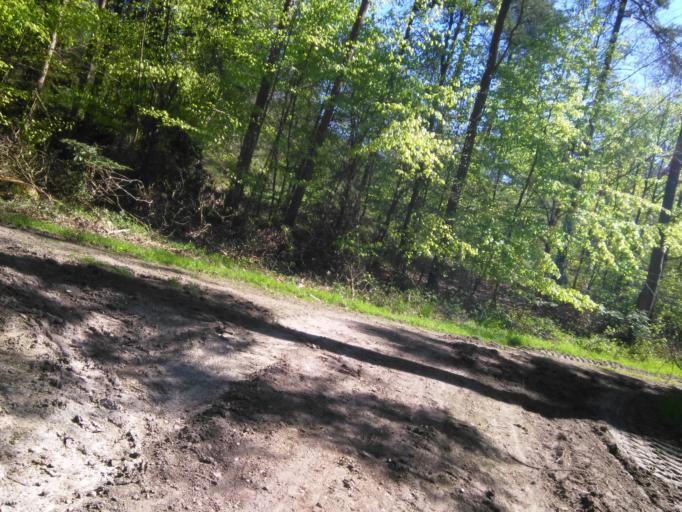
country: DK
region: Central Jutland
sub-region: Odder Kommune
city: Odder
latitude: 55.8920
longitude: 10.0761
